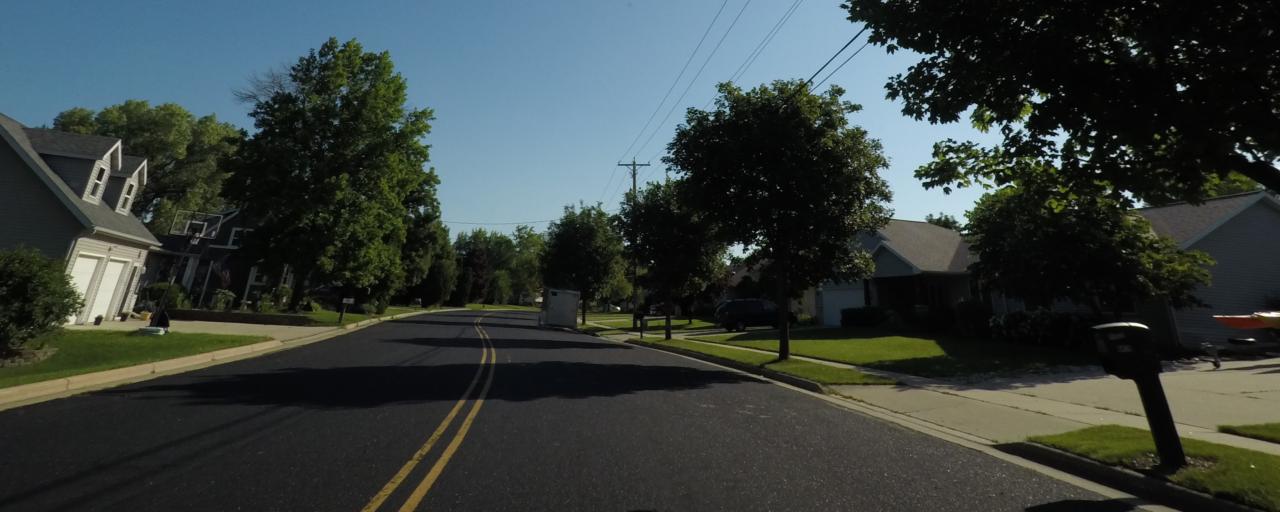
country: US
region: Wisconsin
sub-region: Dane County
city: McFarland
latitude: 43.0048
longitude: -89.3016
